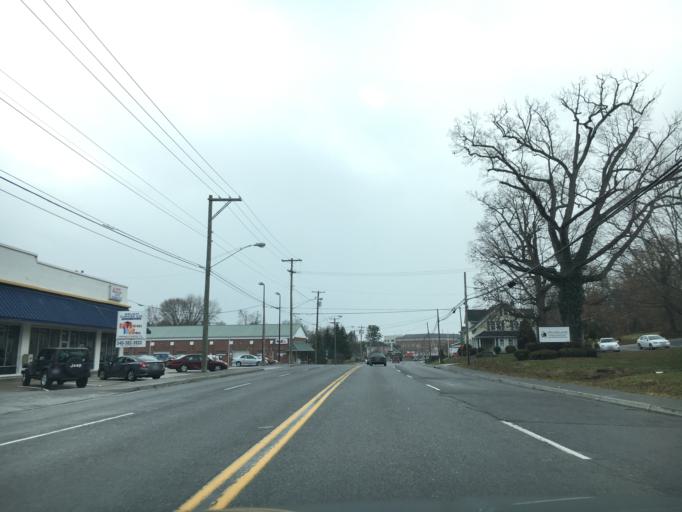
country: US
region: Virginia
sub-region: Montgomery County
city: Christiansburg
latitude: 37.1303
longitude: -80.3998
